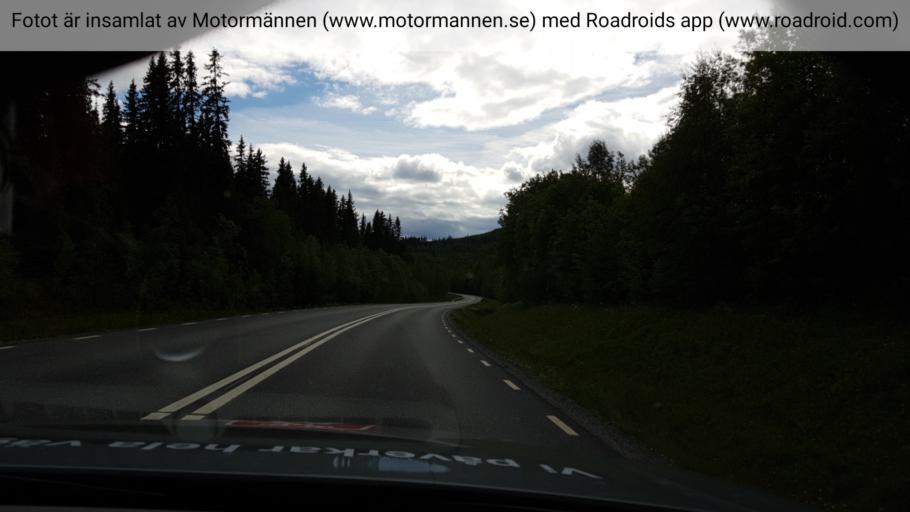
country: SE
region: Jaemtland
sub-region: Stroemsunds Kommun
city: Stroemsund
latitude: 64.0962
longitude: 15.5783
